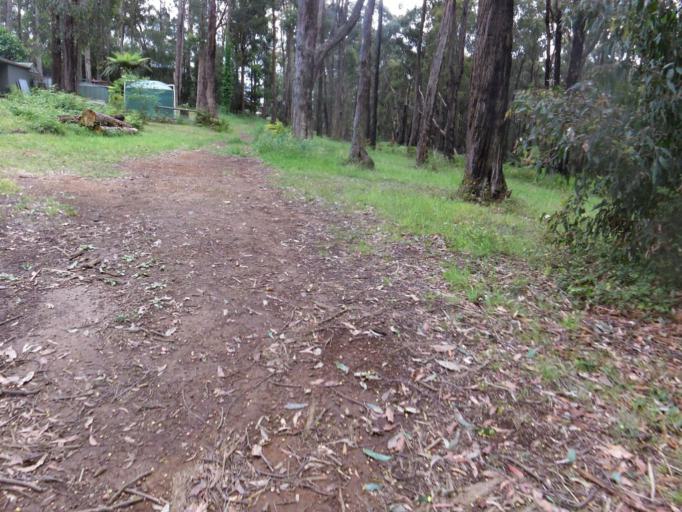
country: AU
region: Victoria
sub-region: Cardinia
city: Cockatoo
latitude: -37.9379
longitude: 145.4707
